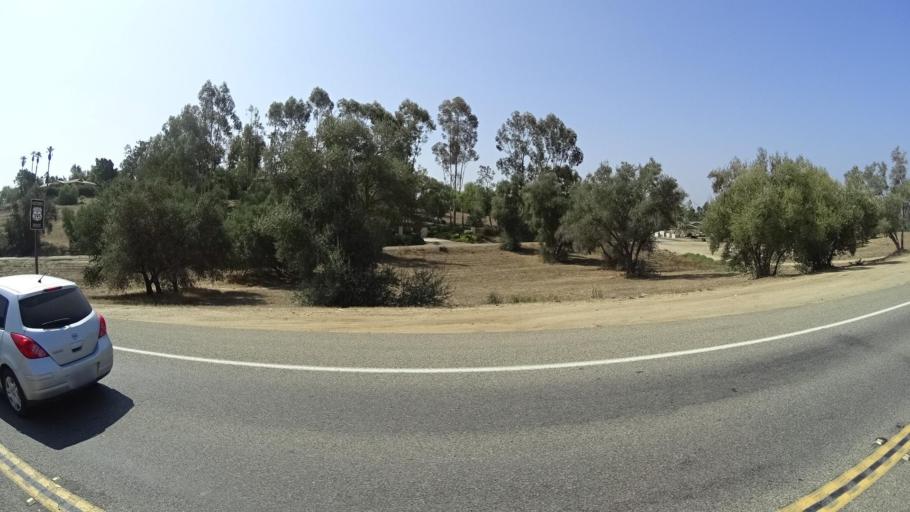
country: US
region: California
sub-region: San Diego County
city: Rainbow
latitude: 33.3911
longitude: -117.1881
